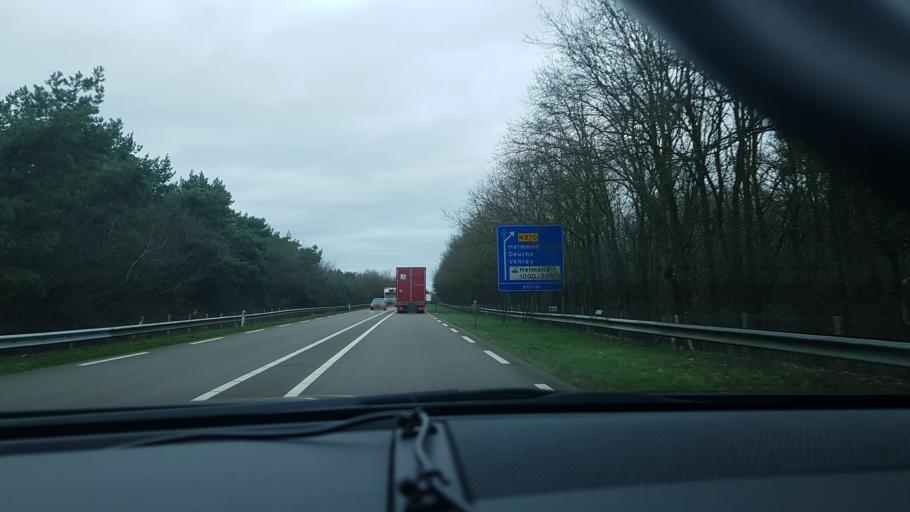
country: NL
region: North Brabant
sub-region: Gemeente Helmond
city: Helmond
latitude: 51.4644
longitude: 5.7172
